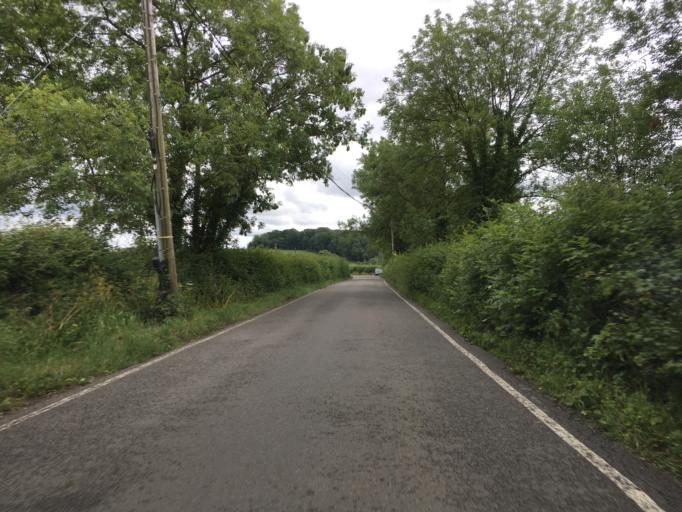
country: GB
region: England
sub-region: Gloucestershire
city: Cinderford
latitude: 51.7888
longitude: -2.4050
